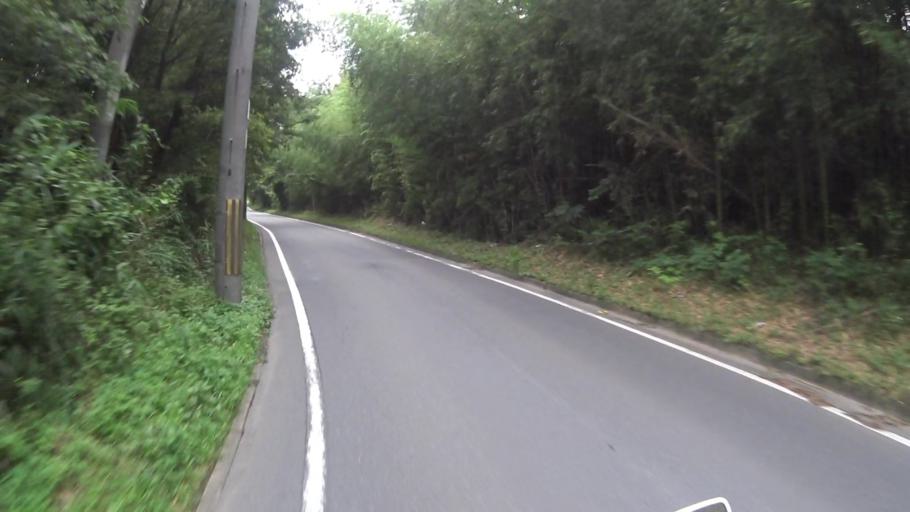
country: JP
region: Kyoto
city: Tanabe
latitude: 34.7749
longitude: 135.7639
